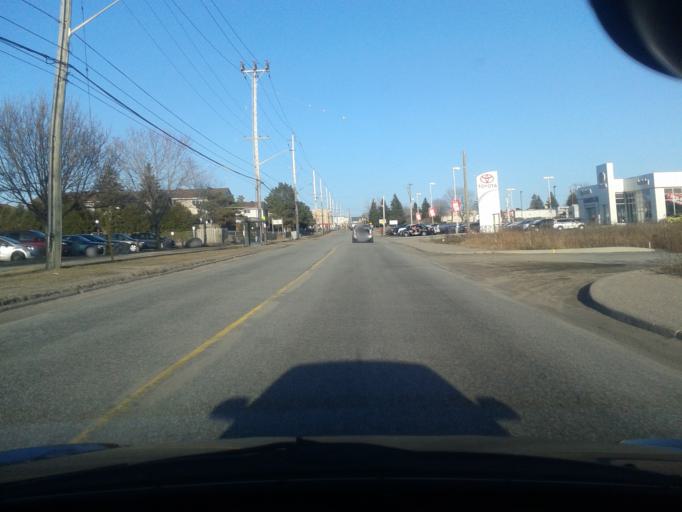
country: CA
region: Ontario
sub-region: Nipissing District
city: North Bay
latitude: 46.3325
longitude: -79.4796
